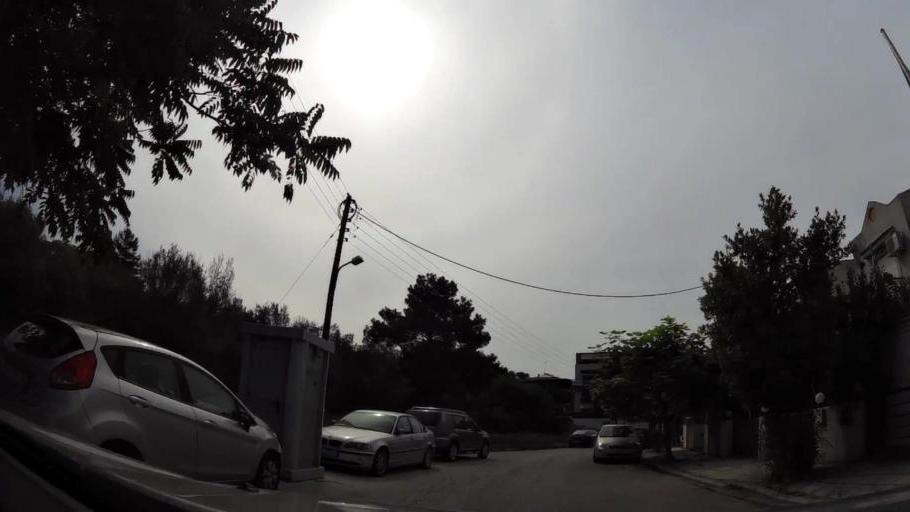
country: GR
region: Central Macedonia
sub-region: Nomos Thessalonikis
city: Panorama
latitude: 40.5870
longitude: 23.0170
